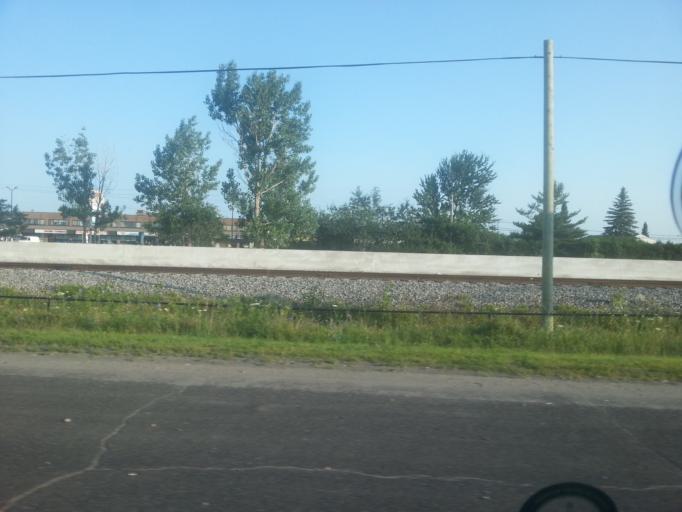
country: CA
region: Quebec
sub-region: Outaouais
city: Gatineau
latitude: 45.4753
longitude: -75.7066
